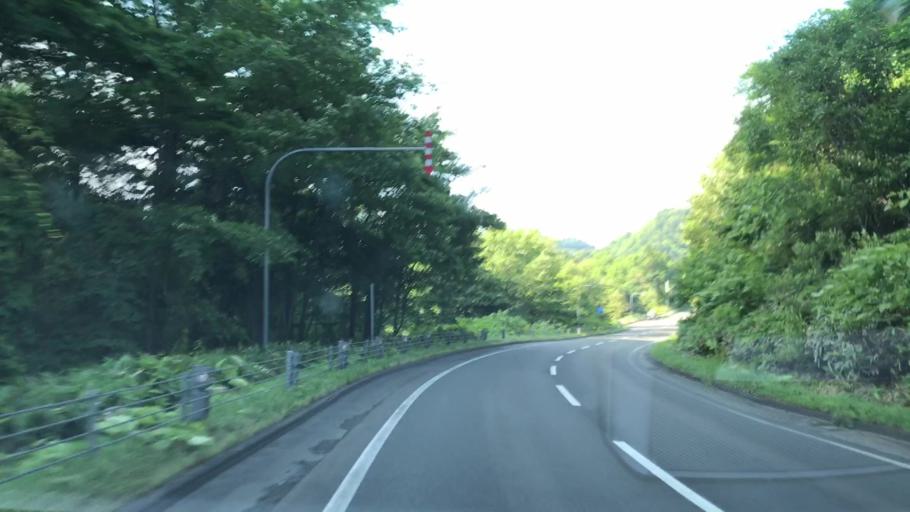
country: JP
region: Hokkaido
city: Iwamizawa
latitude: 42.8985
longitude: 142.1258
